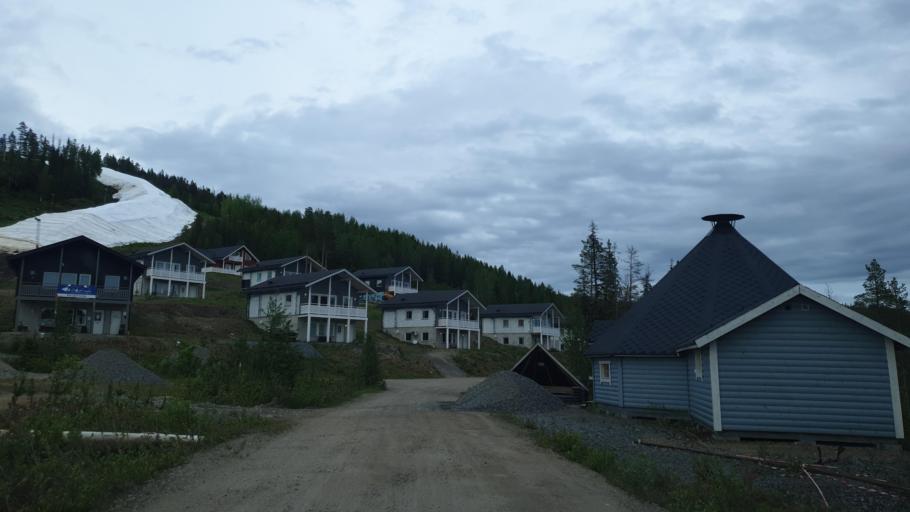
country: SE
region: Norrbotten
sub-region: Jokkmokks Kommun
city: Jokkmokk
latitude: 66.1546
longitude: 19.9920
